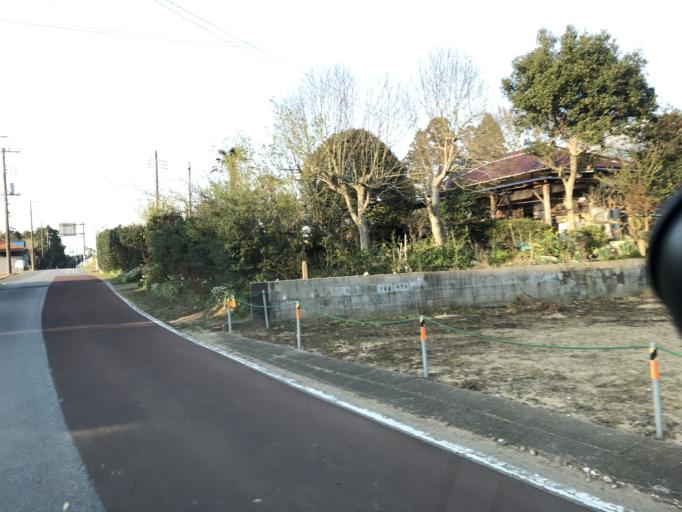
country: JP
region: Chiba
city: Yokaichiba
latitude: 35.7829
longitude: 140.5353
